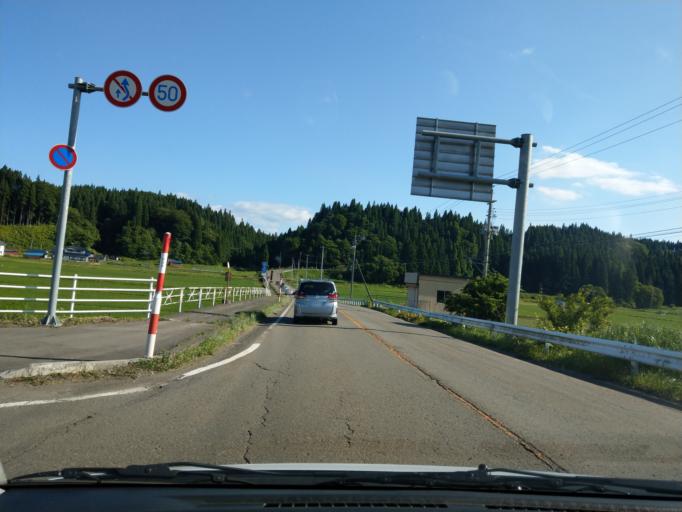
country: JP
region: Akita
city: Takanosu
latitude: 40.1729
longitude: 140.3998
